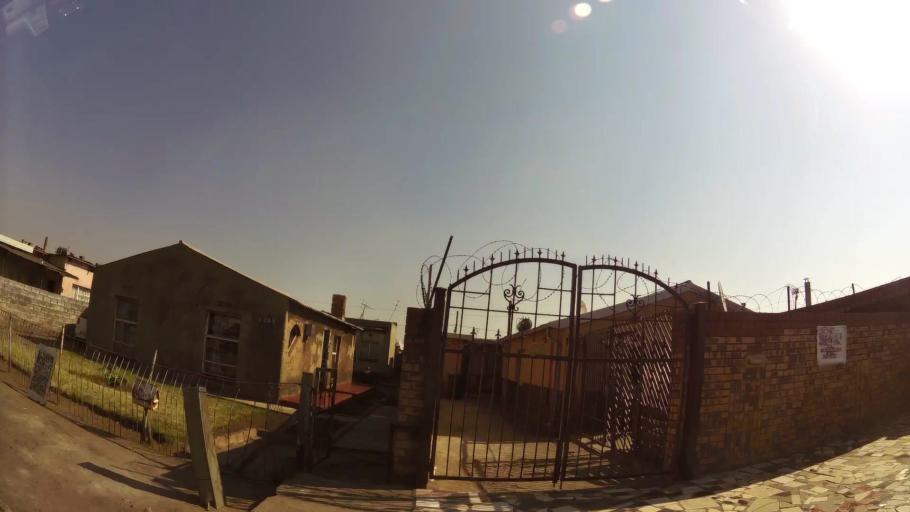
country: ZA
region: Gauteng
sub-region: Ekurhuleni Metropolitan Municipality
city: Boksburg
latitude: -26.2259
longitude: 28.2976
